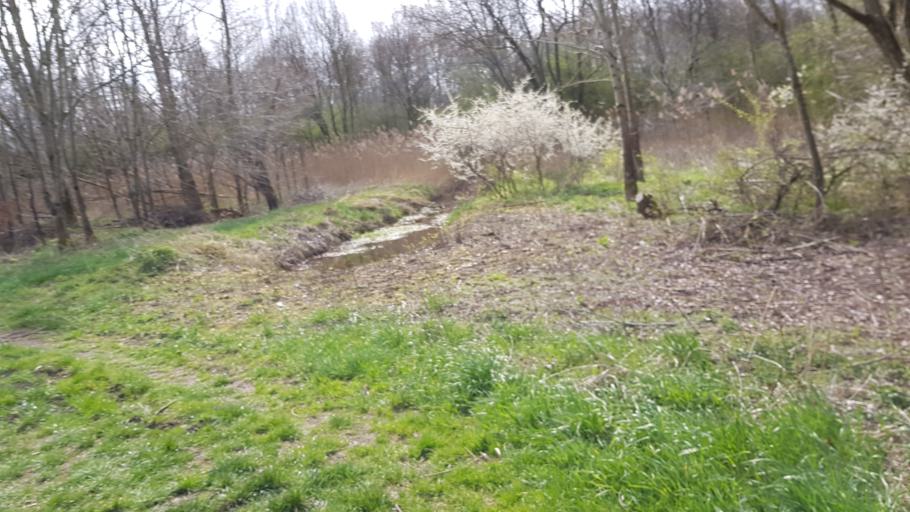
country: NL
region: Utrecht
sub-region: Gemeente Lopik
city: Lopik
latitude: 51.9616
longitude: 5.0043
